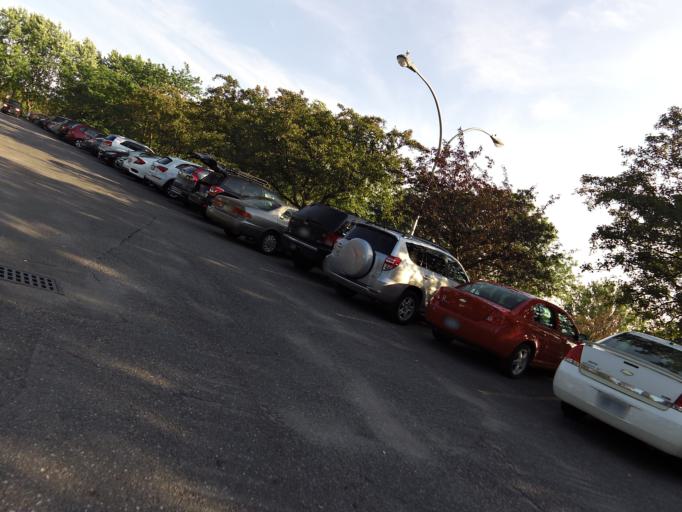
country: CA
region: Ontario
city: Ottawa
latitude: 45.3679
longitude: -75.6912
